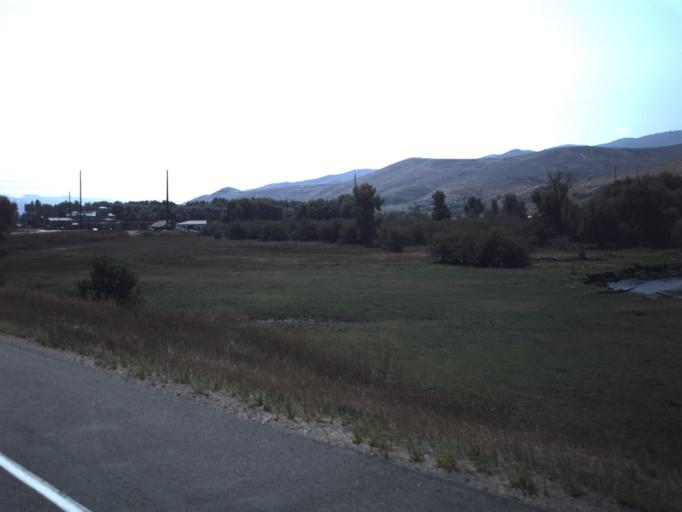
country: US
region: Utah
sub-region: Summit County
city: Coalville
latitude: 40.9156
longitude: -111.4055
